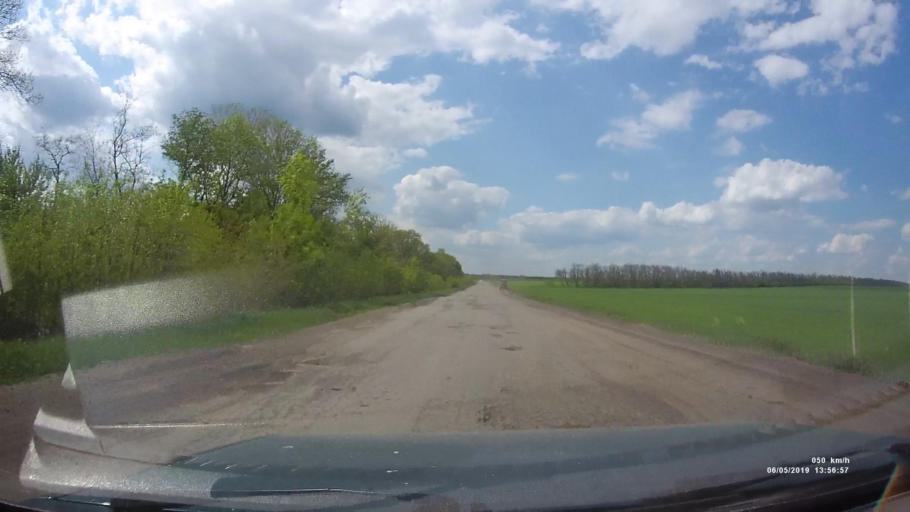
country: RU
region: Rostov
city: Melikhovskaya
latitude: 47.6830
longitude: 40.4265
